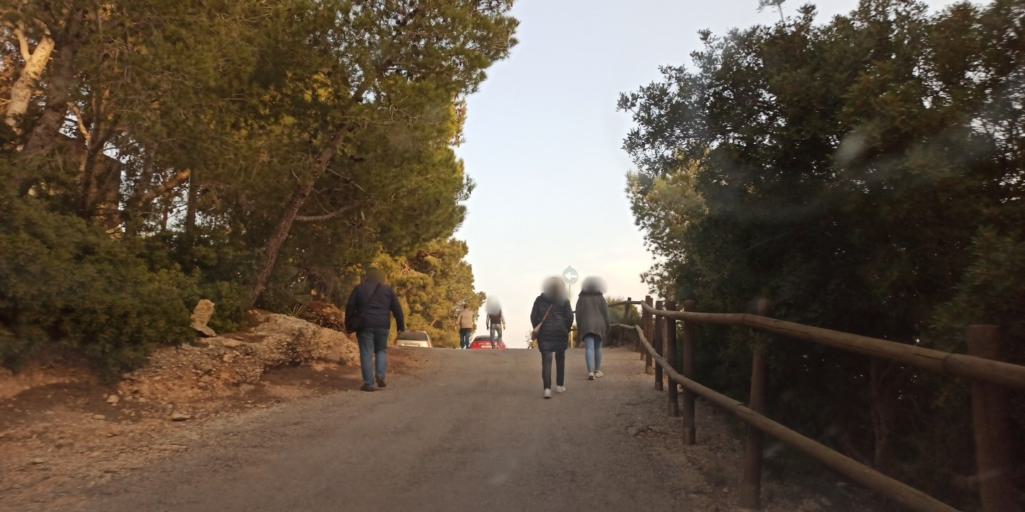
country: ES
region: Catalonia
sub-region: Provincia de Tarragona
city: L'Ampolla
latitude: 40.8138
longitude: 0.7179
